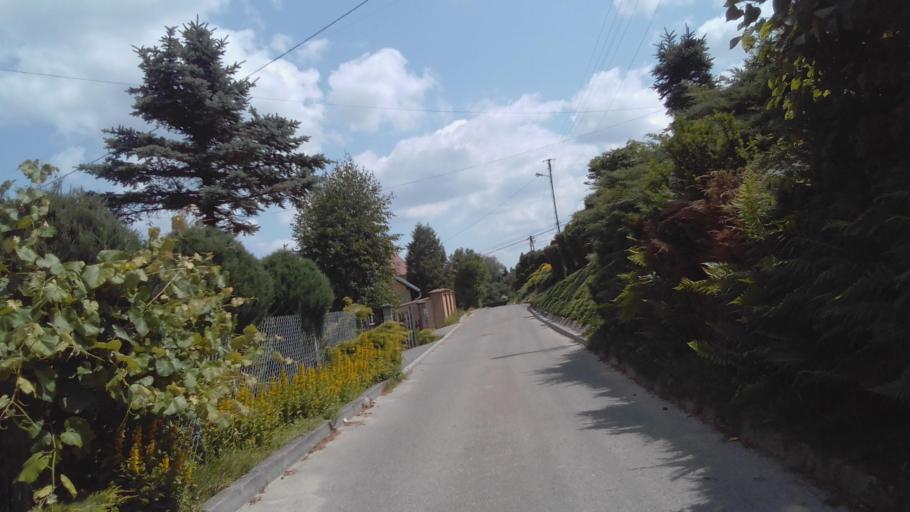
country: PL
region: Subcarpathian Voivodeship
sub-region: Powiat strzyzowski
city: Strzyzow
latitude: 49.8603
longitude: 21.7867
